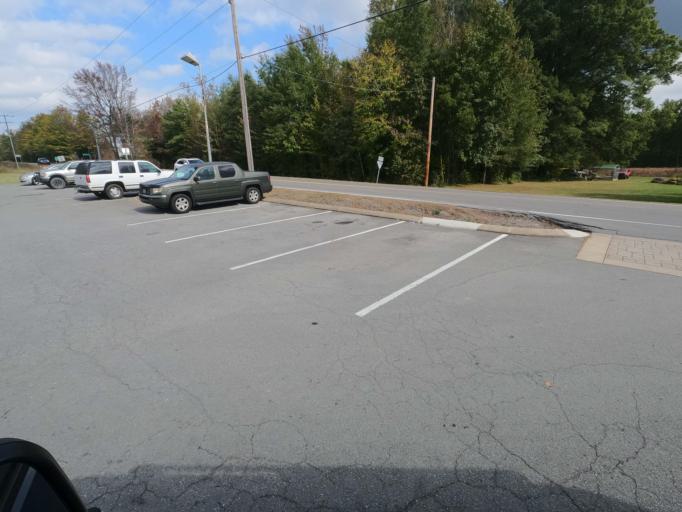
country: US
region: Tennessee
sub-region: Cheatham County
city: Pleasant View
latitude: 36.4435
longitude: -87.1020
